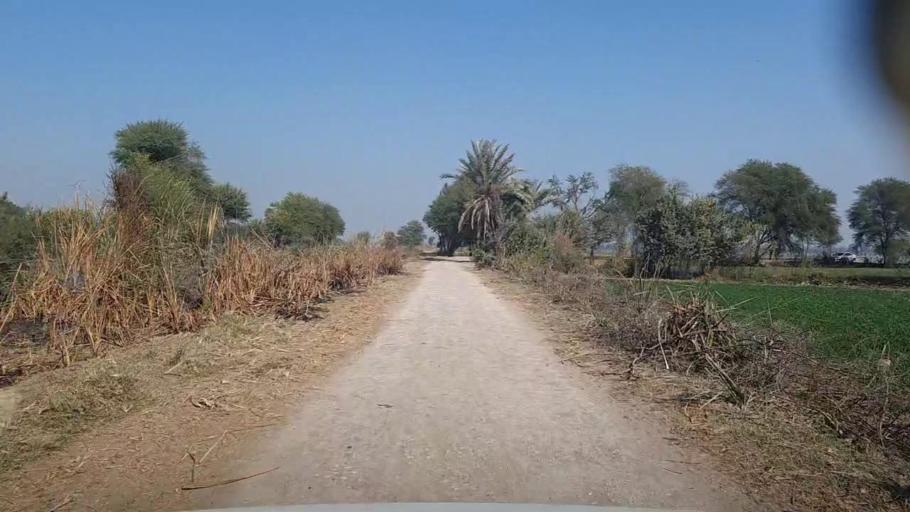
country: PK
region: Sindh
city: Khairpur
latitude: 27.9773
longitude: 69.7107
